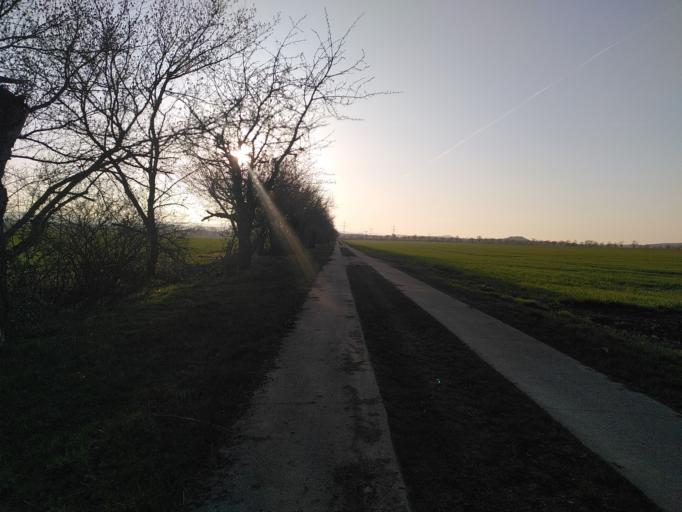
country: DE
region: Saxony-Anhalt
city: Ditfurt
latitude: 51.7957
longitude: 11.2154
